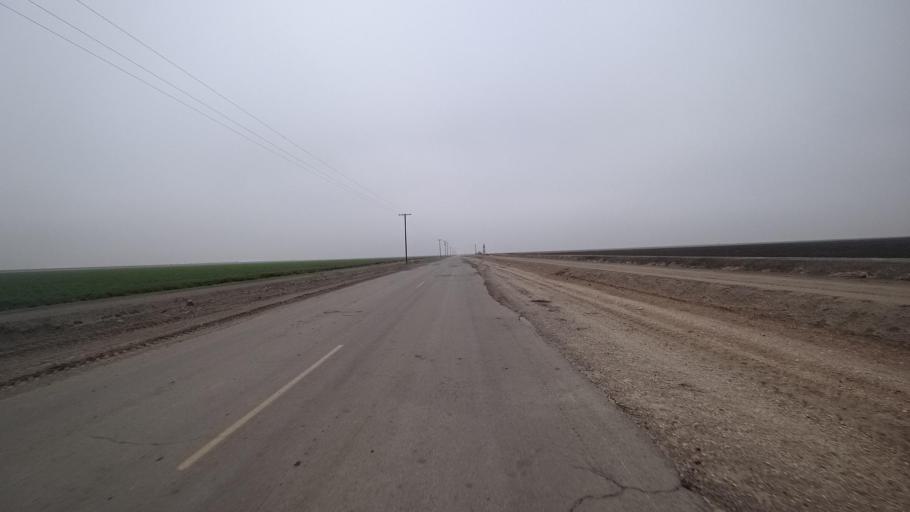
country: US
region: California
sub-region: Kern County
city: Rosedale
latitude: 35.1944
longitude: -119.2197
